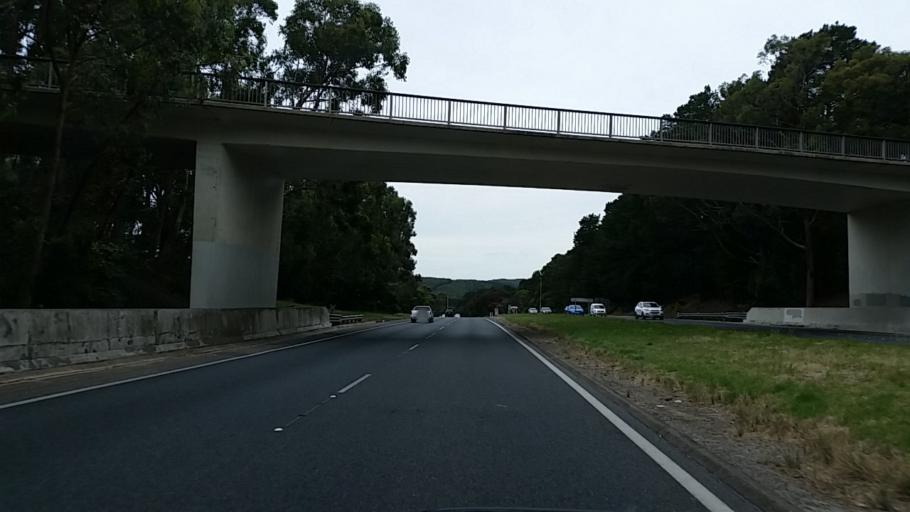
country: AU
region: South Australia
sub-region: Adelaide Hills
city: Aldgate
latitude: -34.9991
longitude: 138.7254
